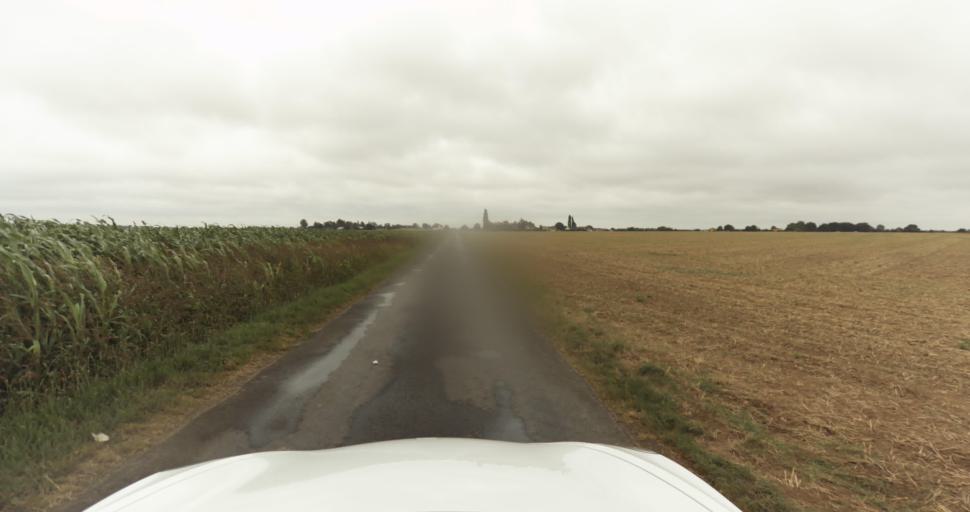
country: FR
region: Haute-Normandie
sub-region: Departement de l'Eure
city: Aviron
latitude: 49.0752
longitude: 1.0711
